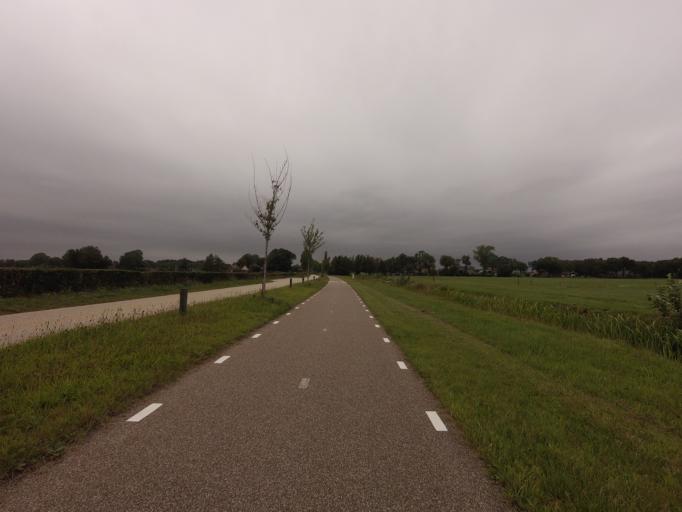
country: NL
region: Friesland
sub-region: Gemeente Opsterland
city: Gorredijk
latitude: 53.0152
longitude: 6.0297
